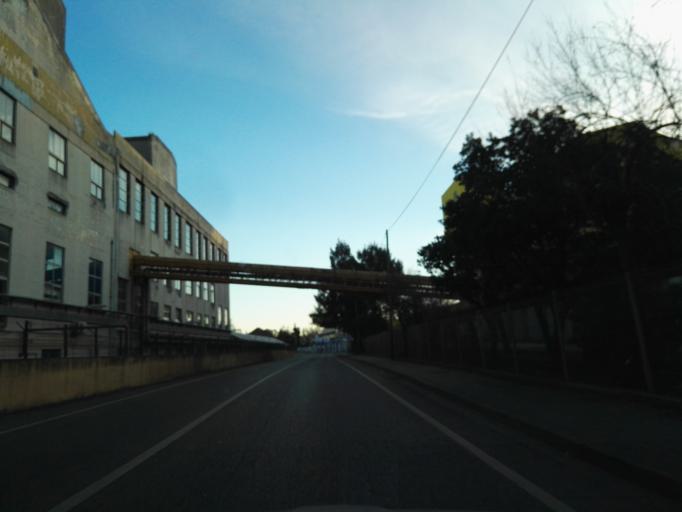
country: PT
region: Lisbon
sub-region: Loures
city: Sao Joao da Talha
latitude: 38.8332
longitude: -9.0854
